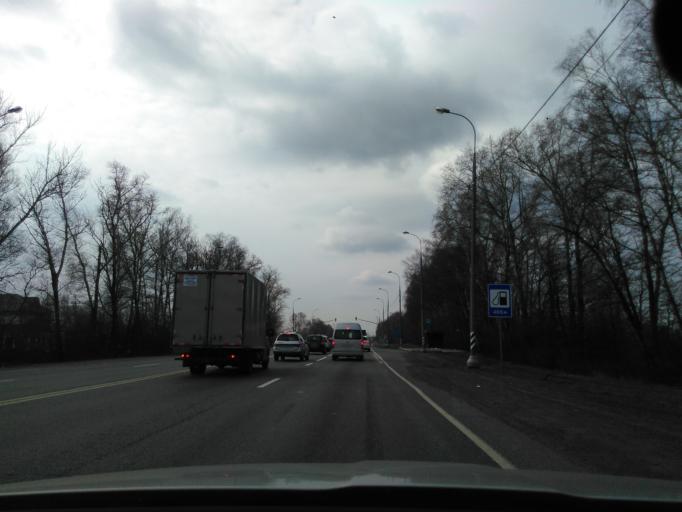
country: RU
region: Moskovskaya
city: Sheremet'yevskiy
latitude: 55.9997
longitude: 37.5372
